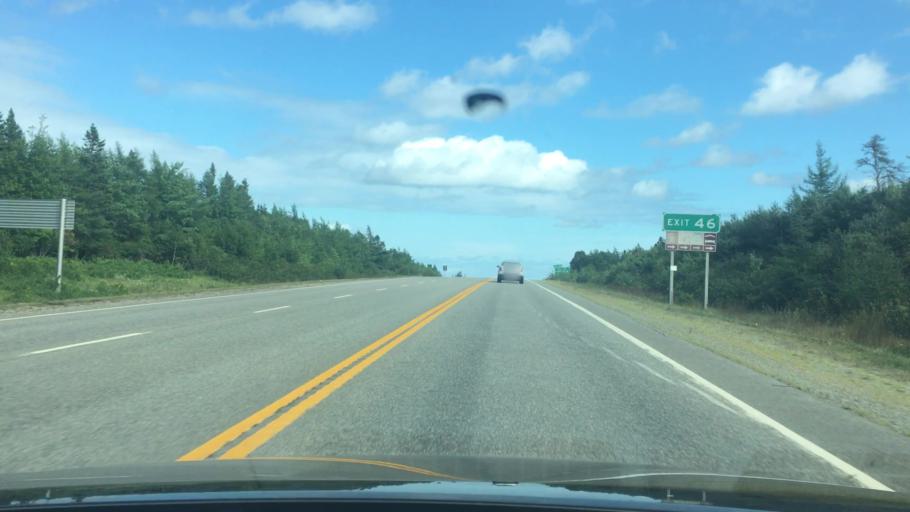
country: CA
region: Nova Scotia
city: Port Hawkesbury
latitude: 45.6147
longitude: -61.0930
